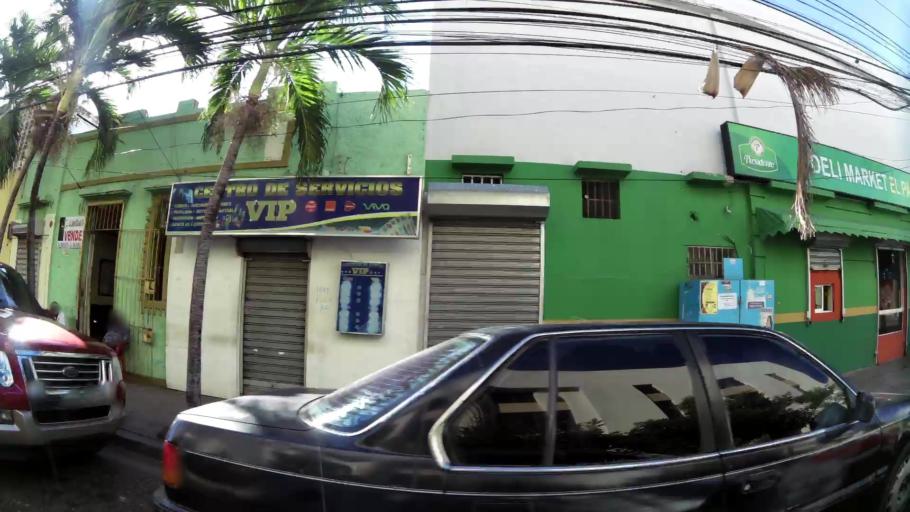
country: DO
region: Nacional
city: Ciudad Nueva
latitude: 18.4670
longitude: -69.8938
